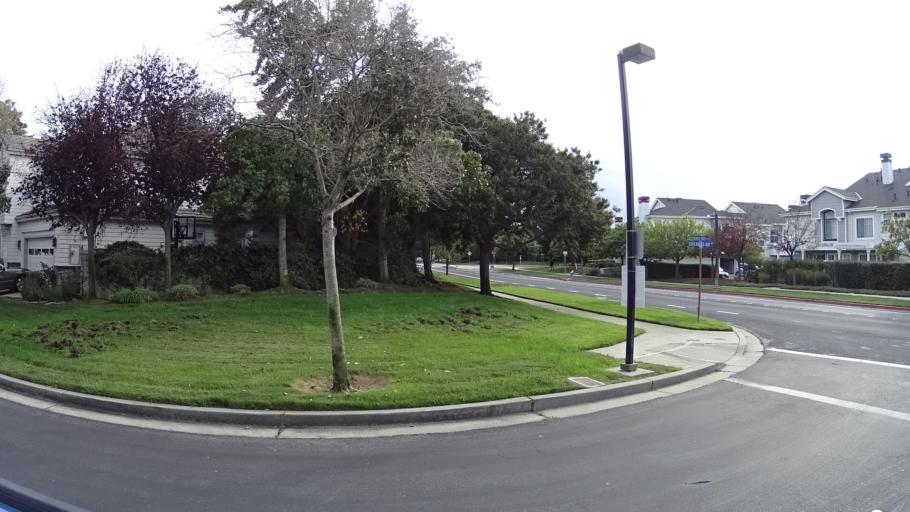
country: US
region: California
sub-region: San Mateo County
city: Redwood Shores
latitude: 37.5407
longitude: -122.2347
